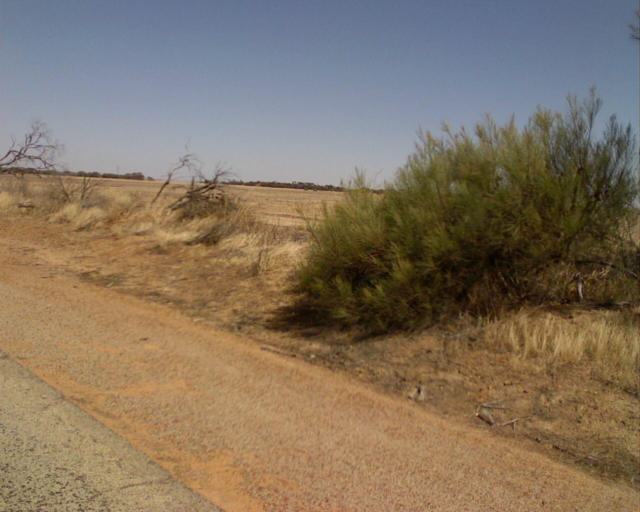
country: AU
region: Western Australia
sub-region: Wongan-Ballidu
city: Wongan Hills
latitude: -30.3834
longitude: 116.9543
